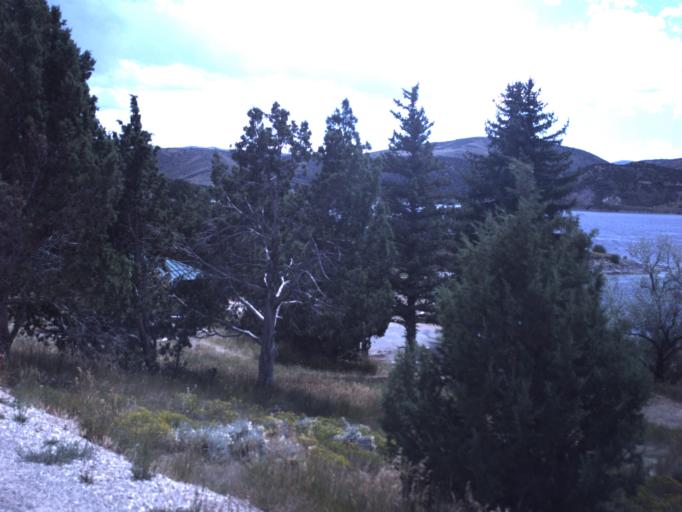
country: US
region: Utah
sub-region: Summit County
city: Oakley
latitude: 40.7825
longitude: -111.3925
